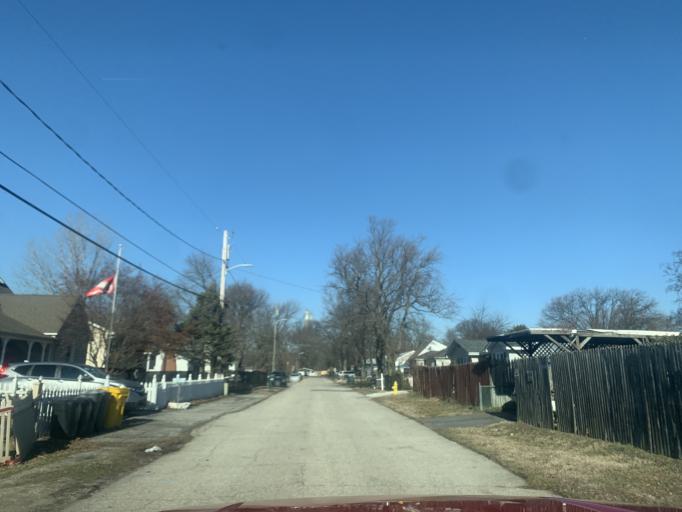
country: US
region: Maryland
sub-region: Anne Arundel County
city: Riviera Beach
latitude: 39.1678
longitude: -76.5267
